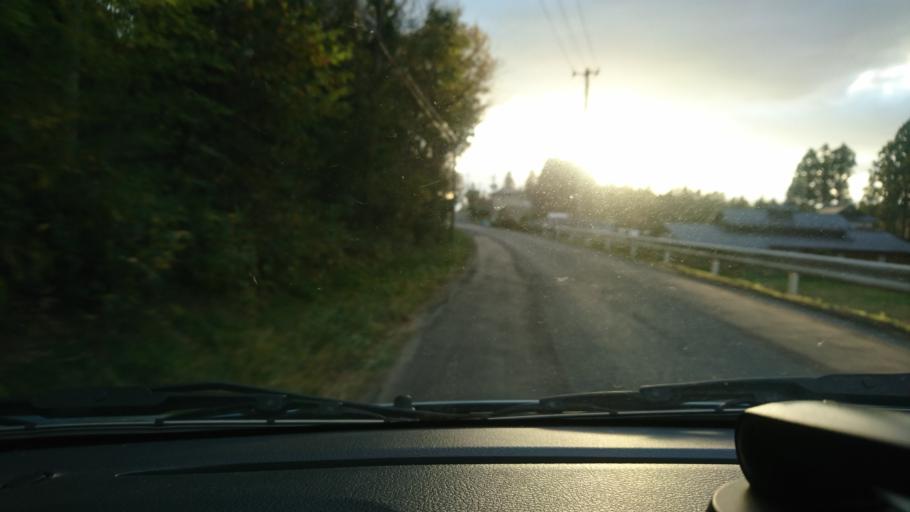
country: JP
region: Iwate
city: Ichinoseki
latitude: 38.7919
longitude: 141.1891
